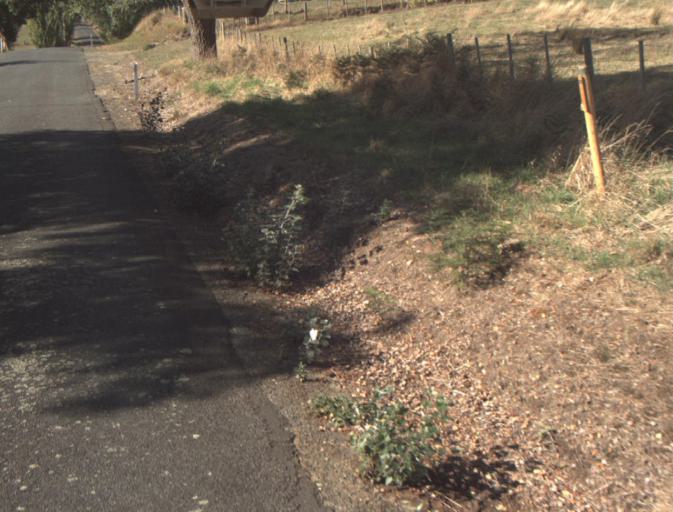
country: AU
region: Tasmania
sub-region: Launceston
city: Mayfield
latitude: -41.2889
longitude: 147.2094
